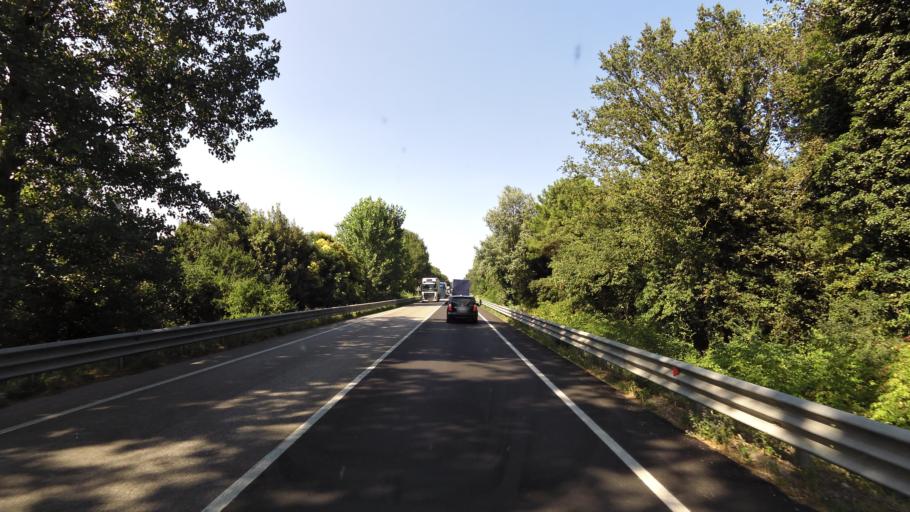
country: IT
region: Emilia-Romagna
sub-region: Provincia di Ravenna
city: Marina Romea
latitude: 44.4850
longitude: 12.2125
